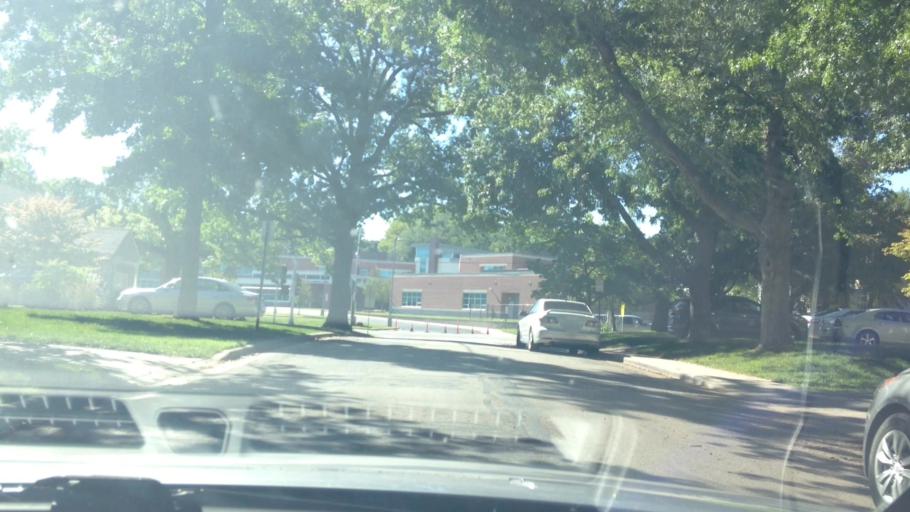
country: US
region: Kansas
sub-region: Johnson County
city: Fairway
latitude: 39.0168
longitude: -94.6389
